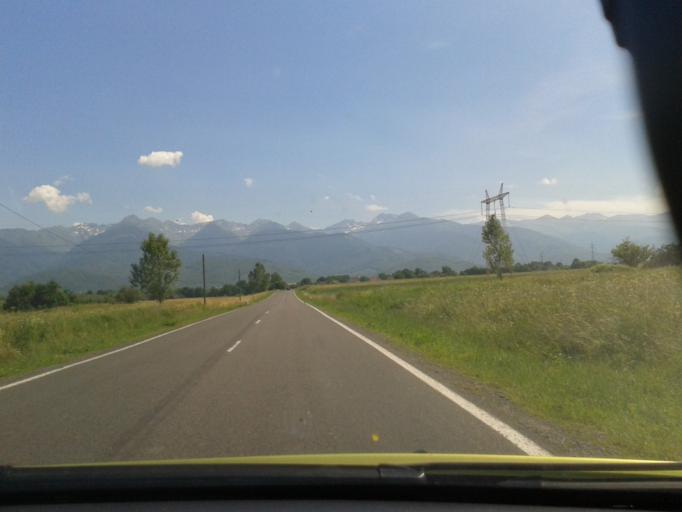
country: RO
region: Sibiu
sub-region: Comuna Cartisoara
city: Cartisoara
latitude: 45.7388
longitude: 24.5746
